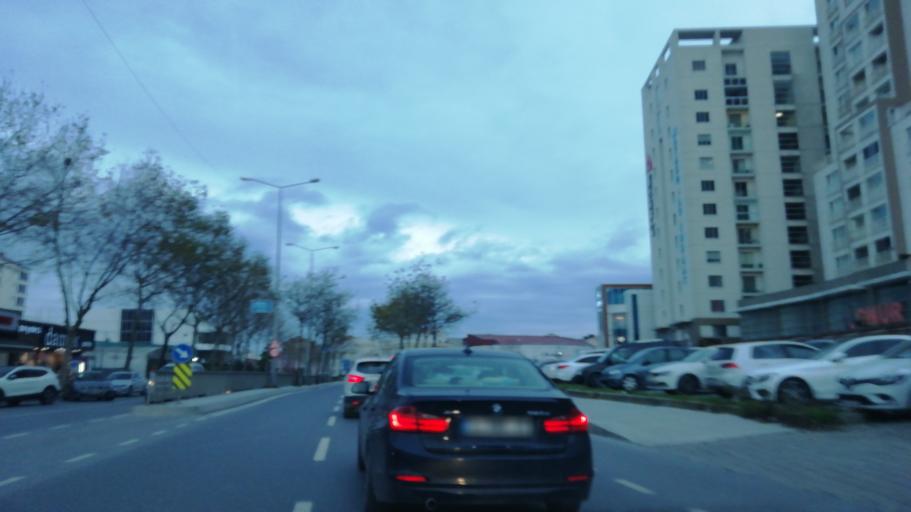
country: TR
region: Istanbul
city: Esenyurt
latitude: 41.0662
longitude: 28.6702
